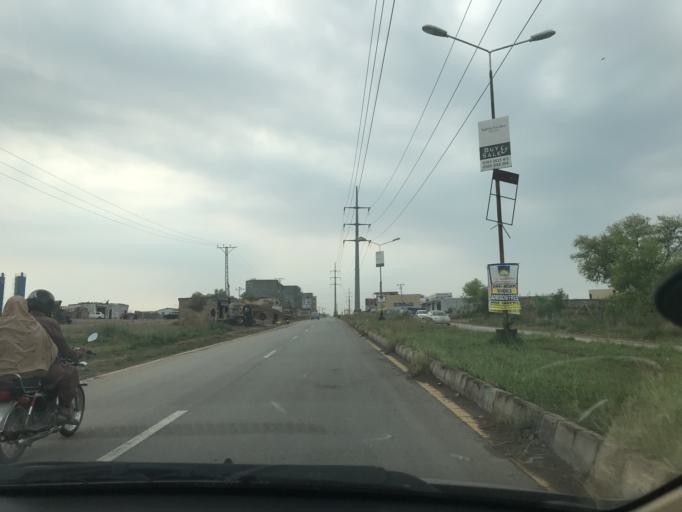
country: PK
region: Islamabad
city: Islamabad
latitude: 33.6872
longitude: 73.1665
